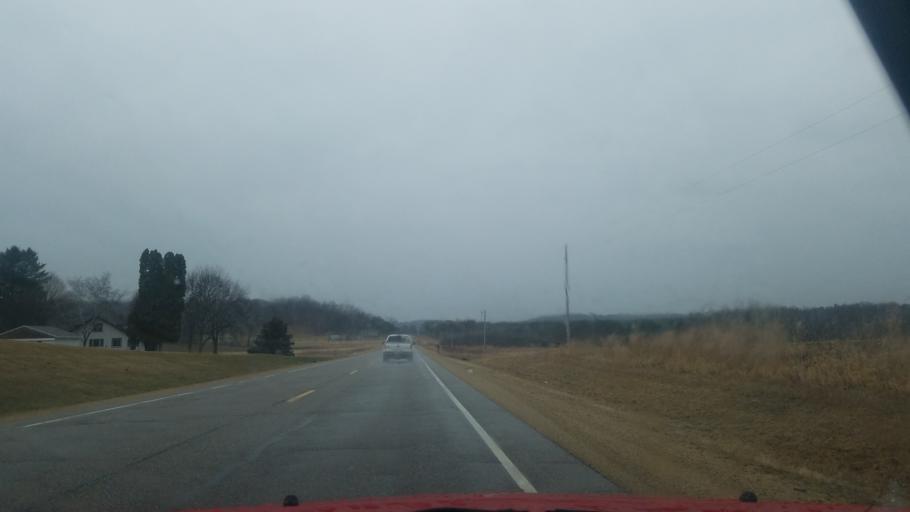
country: US
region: Wisconsin
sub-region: Dunn County
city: Tainter Lake
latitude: 44.9940
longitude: -91.8945
